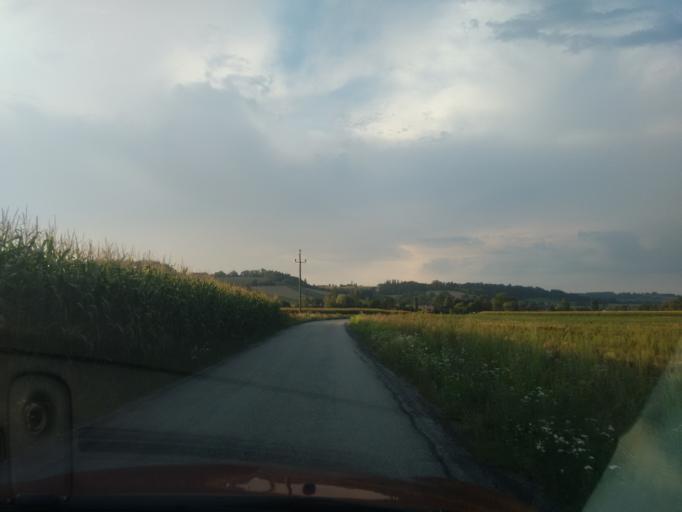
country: AT
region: Upper Austria
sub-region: Politischer Bezirk Grieskirchen
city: Bad Schallerbach
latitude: 48.2015
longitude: 13.9211
